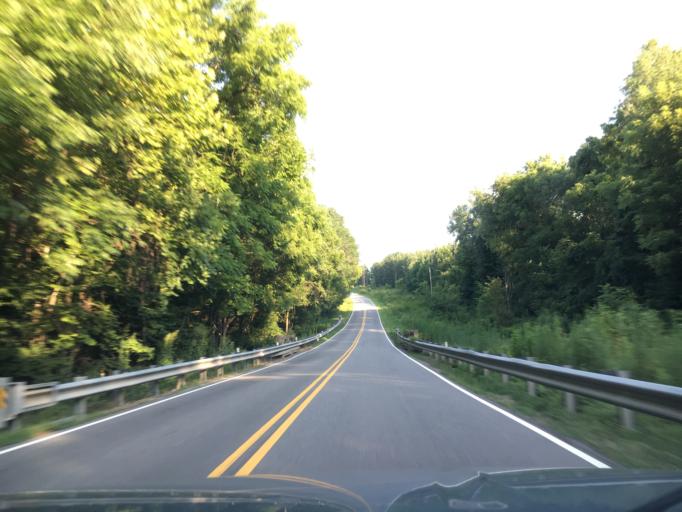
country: US
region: Virginia
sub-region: Pittsylvania County
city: Chatham
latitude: 36.8205
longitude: -79.2741
